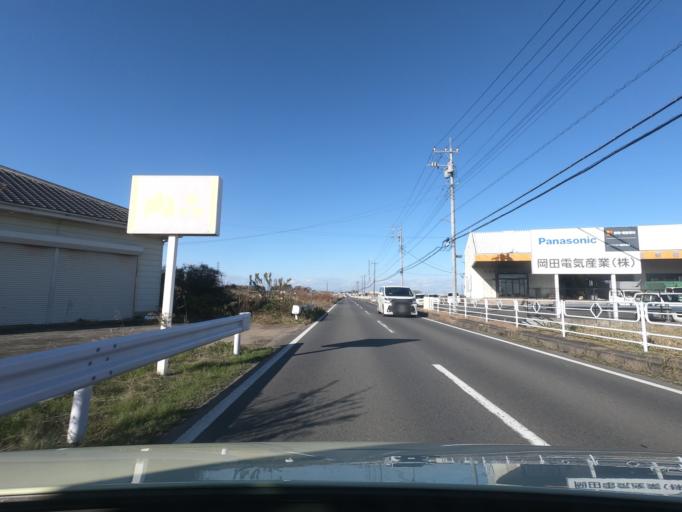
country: JP
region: Ibaraki
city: Ishige
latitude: 36.1669
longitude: 139.9896
